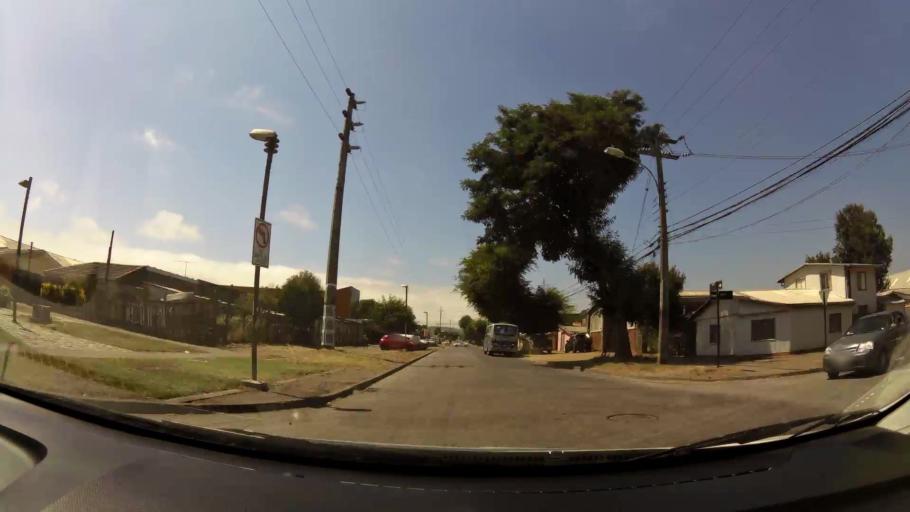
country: CL
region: Biobio
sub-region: Provincia de Concepcion
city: Concepcion
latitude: -36.8092
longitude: -73.0496
